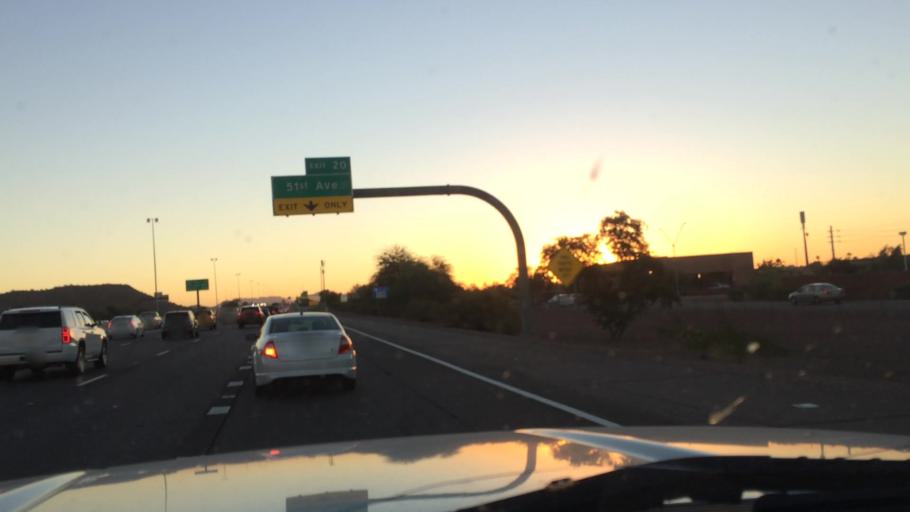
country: US
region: Arizona
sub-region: Maricopa County
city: Peoria
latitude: 33.6695
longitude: -112.1827
